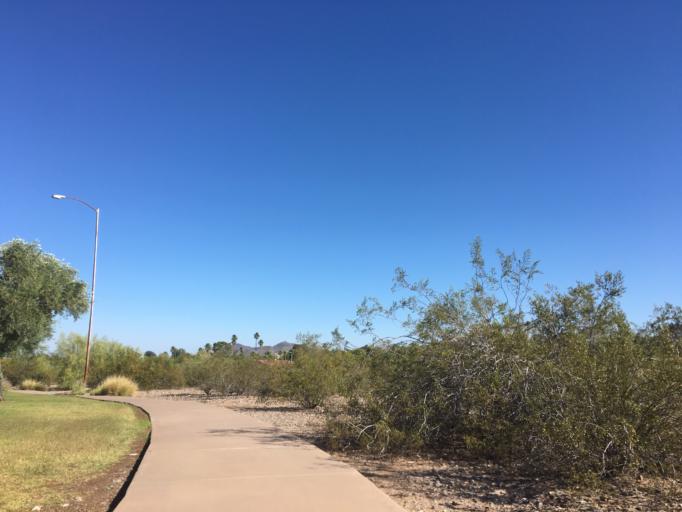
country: US
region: Arizona
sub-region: Maricopa County
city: Paradise Valley
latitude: 33.5333
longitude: -112.0350
